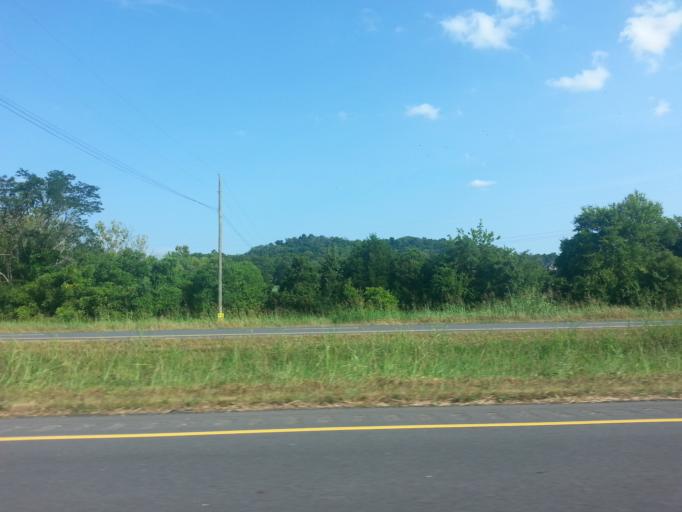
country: US
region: Tennessee
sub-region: Loudon County
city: Greenback
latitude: 35.7463
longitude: -84.1519
